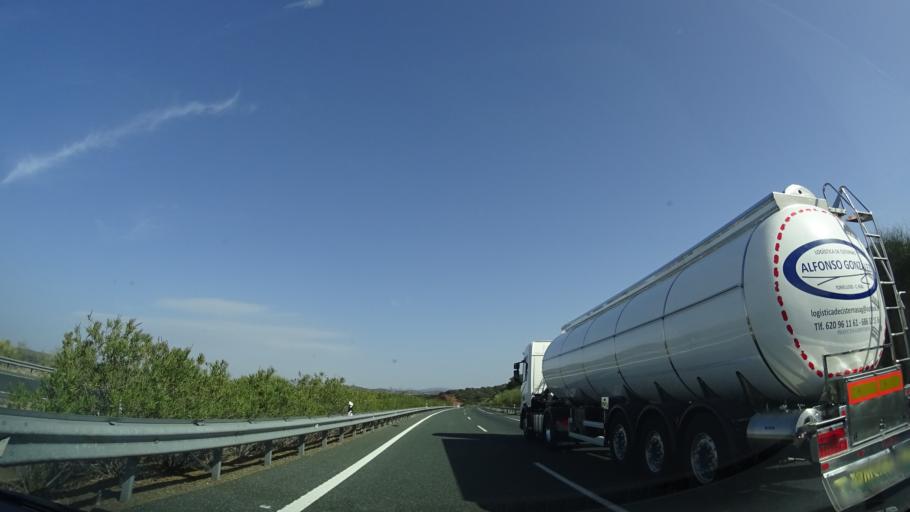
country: ES
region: Andalusia
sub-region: Provincia de Sevilla
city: El Ronquillo
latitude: 37.7208
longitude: -6.1689
